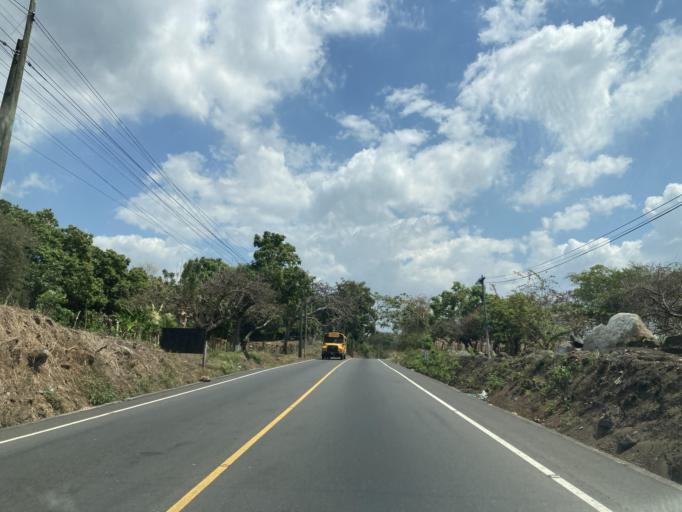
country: GT
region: Santa Rosa
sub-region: Municipio de Taxisco
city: Taxisco
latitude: 14.0661
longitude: -90.4450
